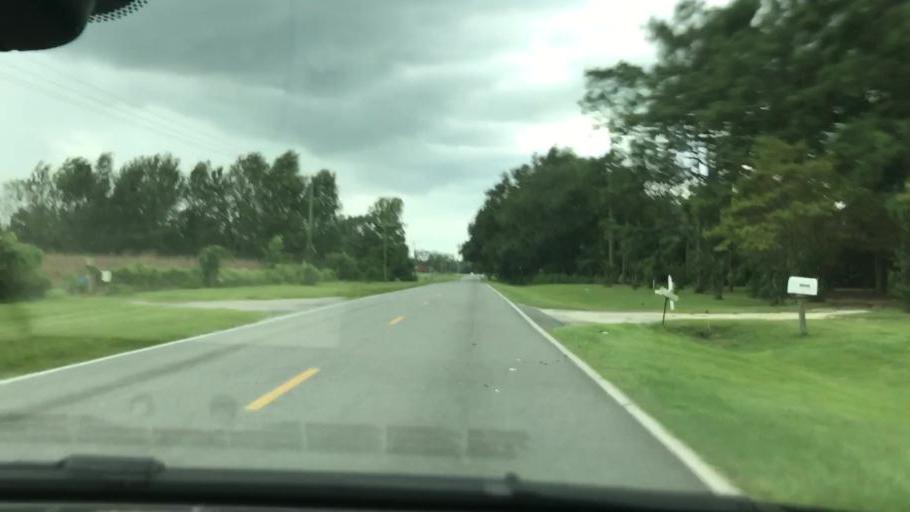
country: US
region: Florida
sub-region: Madison County
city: Madison
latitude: 30.3948
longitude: -83.3004
